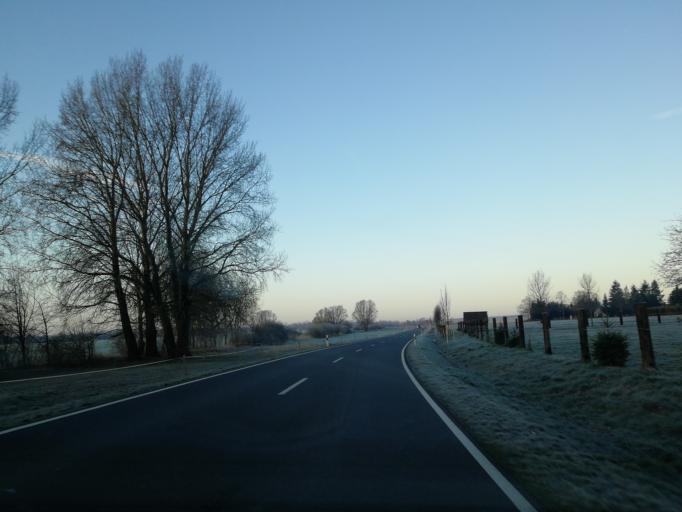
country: DE
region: Brandenburg
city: Finsterwalde
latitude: 51.6854
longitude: 13.7257
